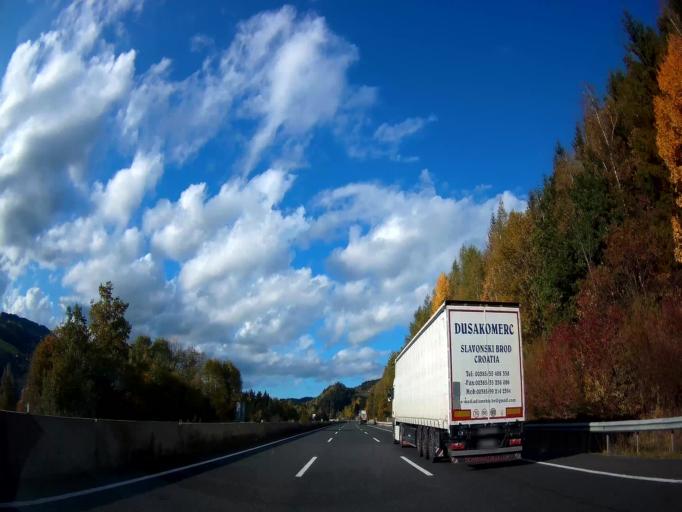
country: AT
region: Carinthia
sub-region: Politischer Bezirk Wolfsberg
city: Wolfsberg
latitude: 46.8790
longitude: 14.8312
